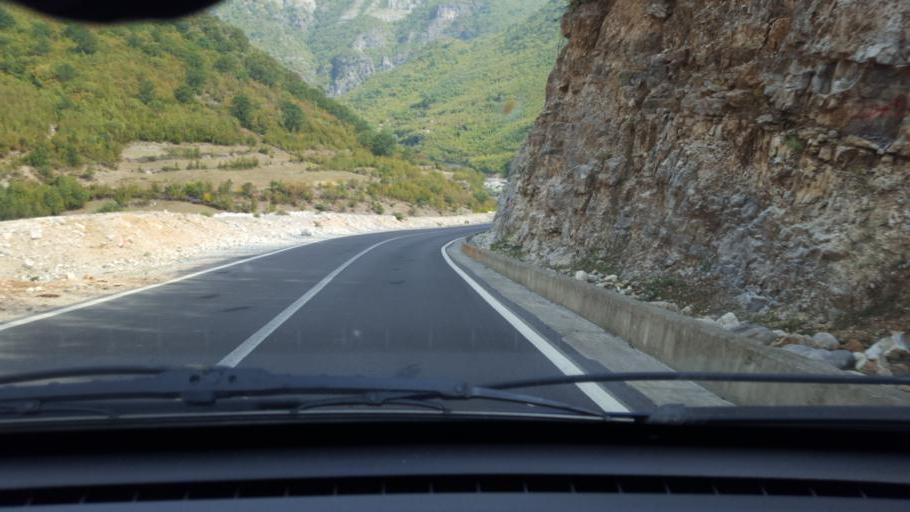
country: AL
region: Shkoder
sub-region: Rrethi i Malesia e Madhe
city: Kastrat
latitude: 42.4281
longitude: 19.5196
